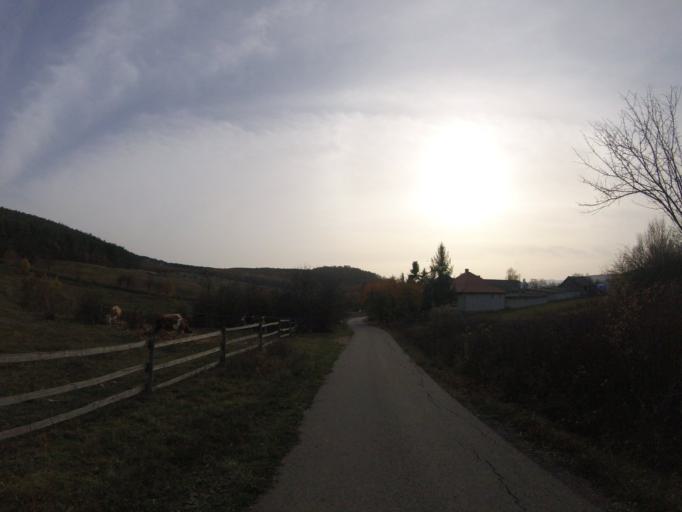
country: HU
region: Borsod-Abauj-Zemplen
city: Gonc
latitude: 48.5156
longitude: 21.4582
